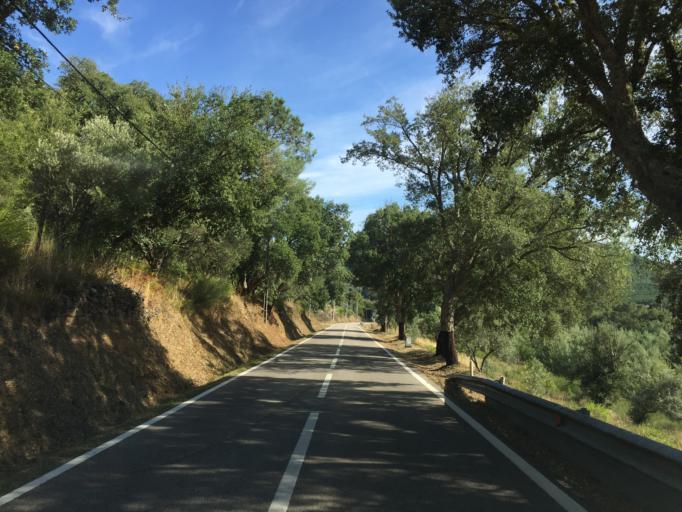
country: PT
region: Portalegre
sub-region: Marvao
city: Marvao
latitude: 39.3901
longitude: -7.3886
